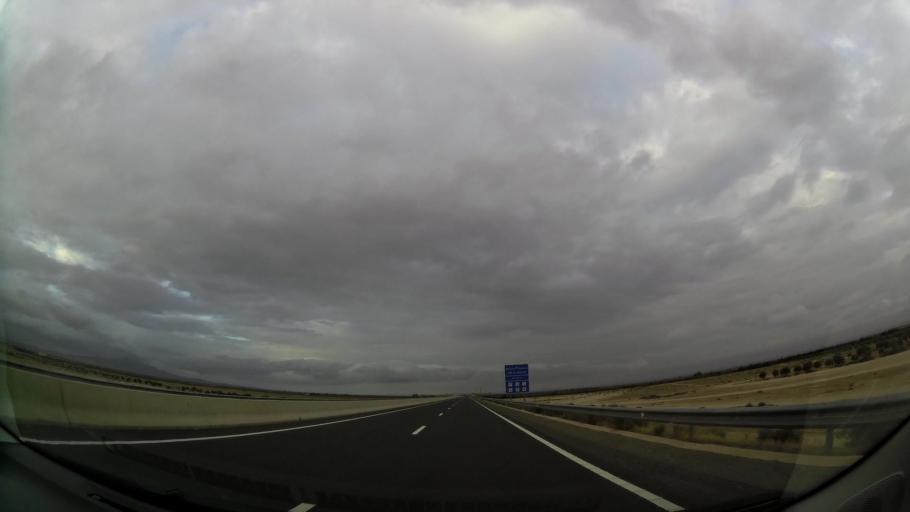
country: MA
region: Taza-Al Hoceima-Taounate
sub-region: Taza
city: Guercif
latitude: 34.3206
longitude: -3.3631
